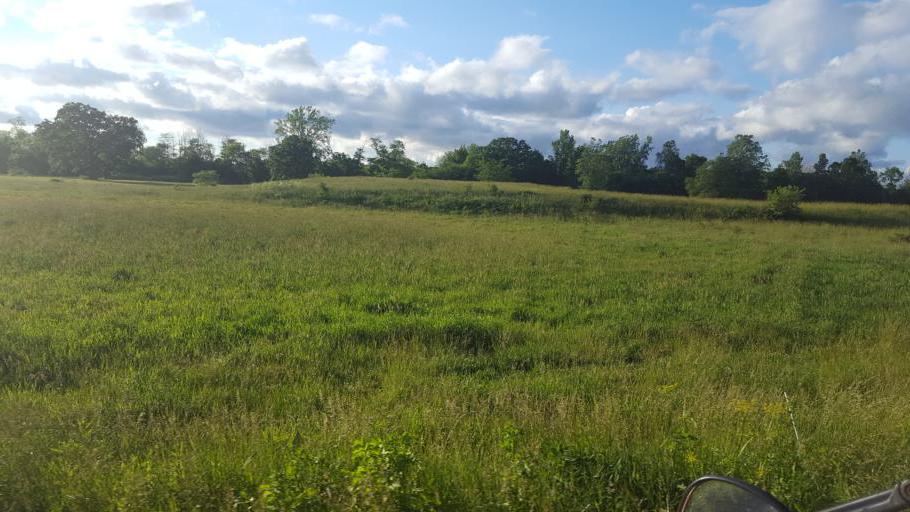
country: US
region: Ohio
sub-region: Knox County
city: Fredericktown
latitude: 40.4577
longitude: -82.6343
